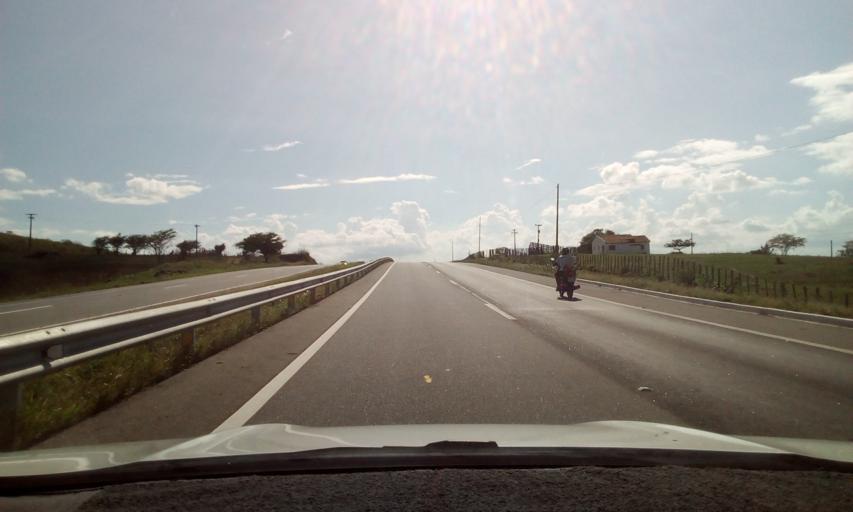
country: BR
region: Paraiba
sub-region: Gurinhem
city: Gurinhem
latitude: -7.1761
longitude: -35.4103
